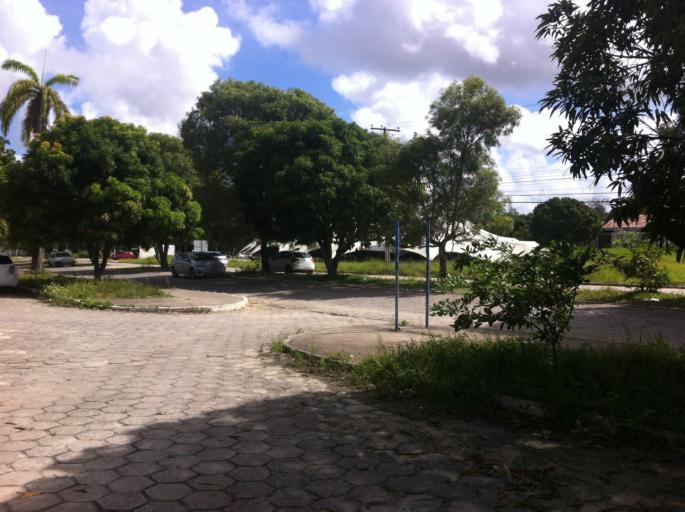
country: BR
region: Alagoas
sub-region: Satuba
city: Satuba
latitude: -9.5569
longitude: -35.7777
